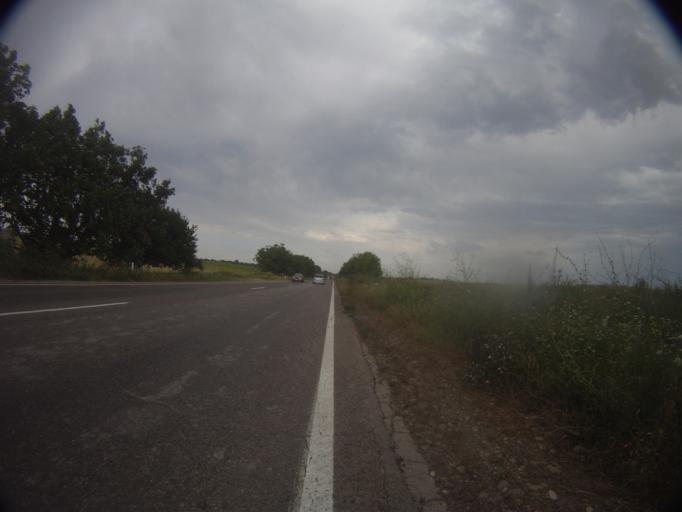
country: GE
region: Kakheti
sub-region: Gurjaani
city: Gurjaani
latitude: 41.6256
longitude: 45.7677
